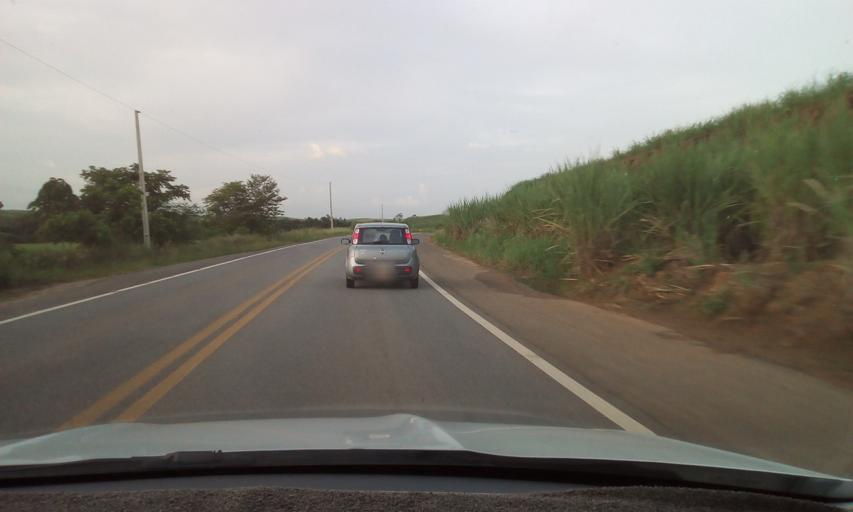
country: BR
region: Pernambuco
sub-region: Vicencia
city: Vicencia
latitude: -7.6355
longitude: -35.2528
